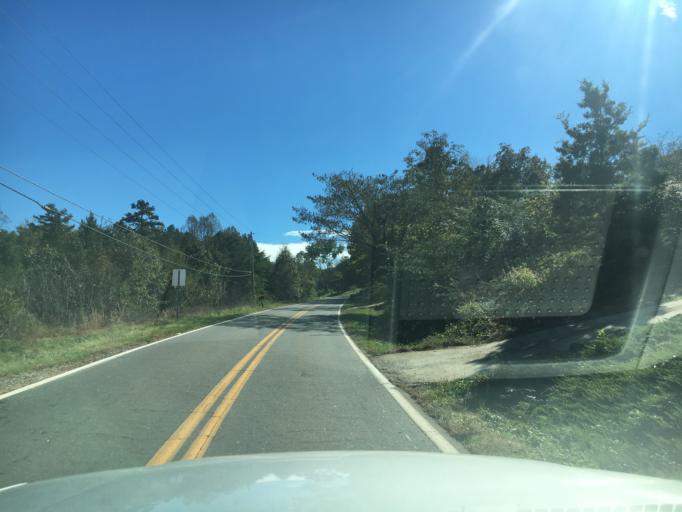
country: US
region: North Carolina
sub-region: Burke County
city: Salem
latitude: 35.7126
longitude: -81.7362
